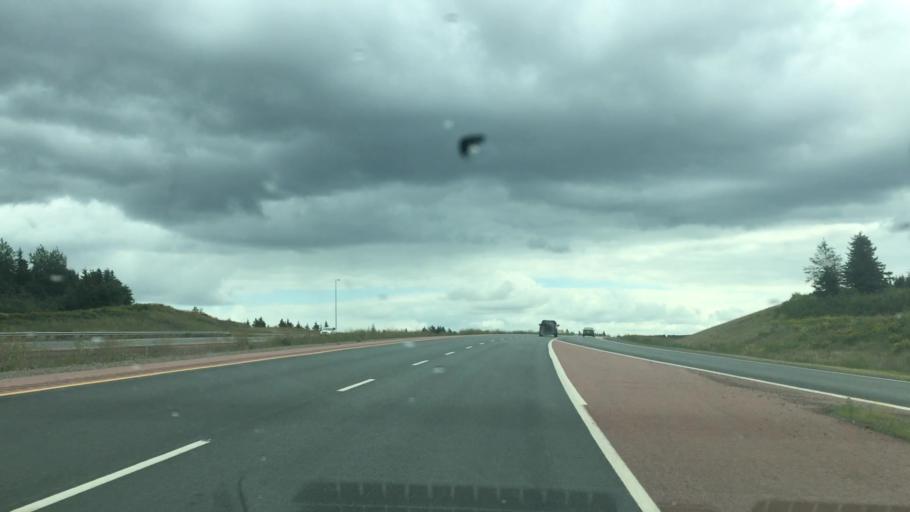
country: CA
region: Nova Scotia
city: Antigonish
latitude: 45.6092
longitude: -61.9635
